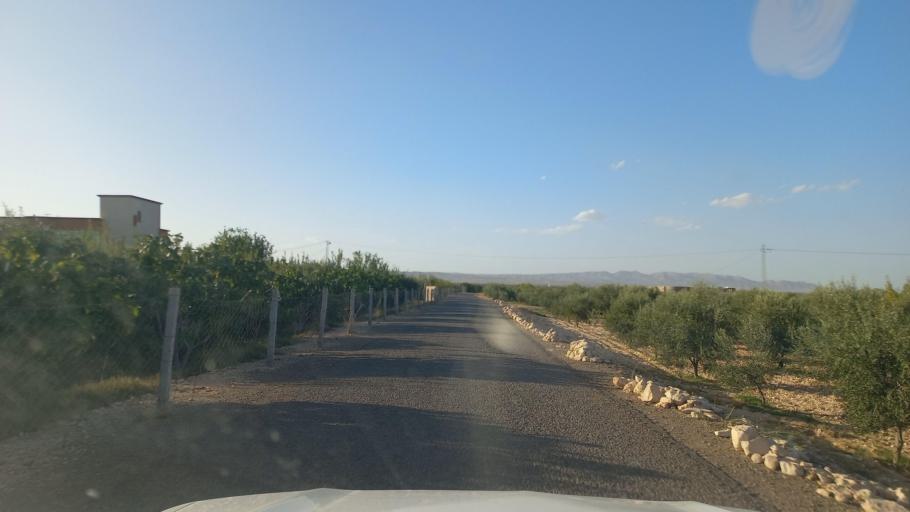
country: TN
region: Al Qasrayn
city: Kasserine
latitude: 35.2787
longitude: 9.0282
